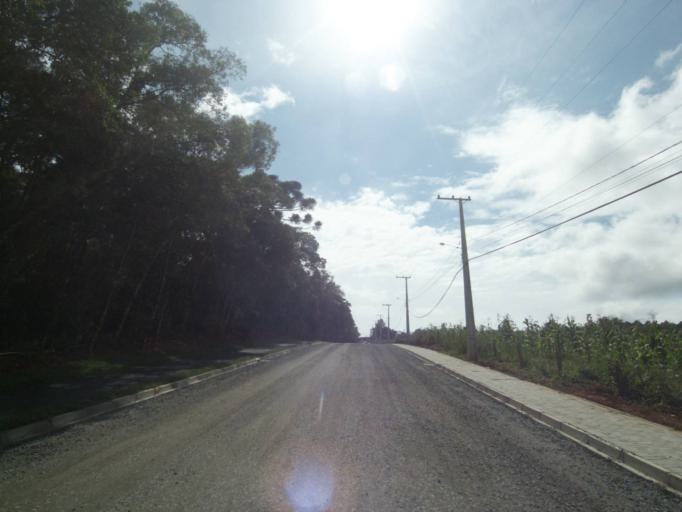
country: BR
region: Parana
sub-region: Quatro Barras
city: Quatro Barras
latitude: -25.3338
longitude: -49.0747
